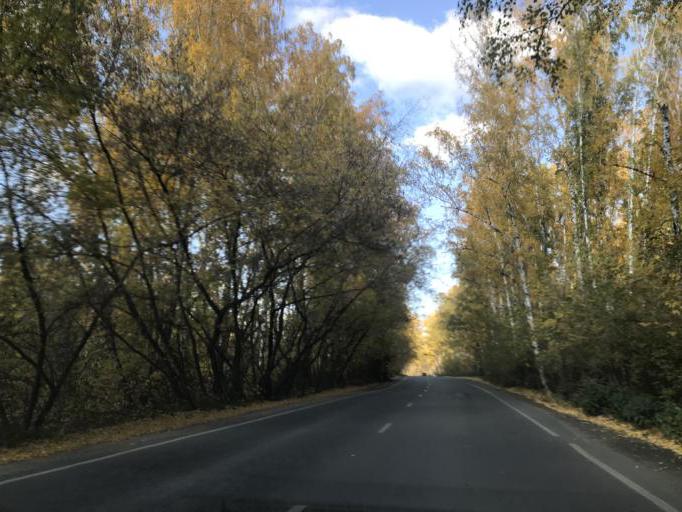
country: RU
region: Chelyabinsk
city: Dolgoderevenskoye
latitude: 55.2594
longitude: 61.3635
